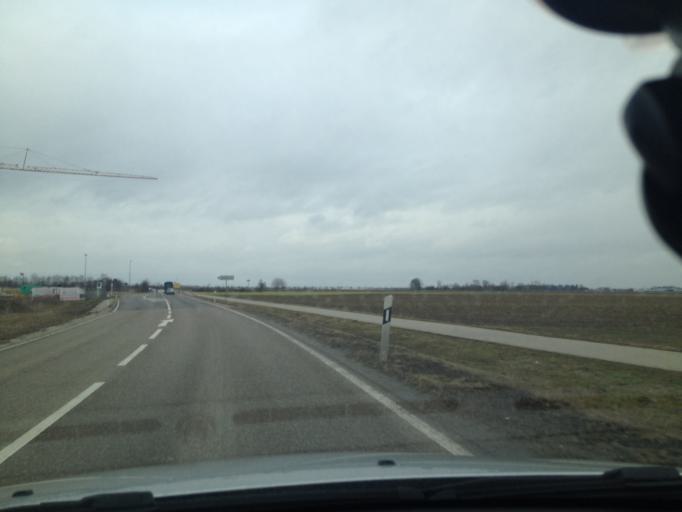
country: DE
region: Bavaria
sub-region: Swabia
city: Stadtbergen
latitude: 48.4023
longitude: 10.8405
